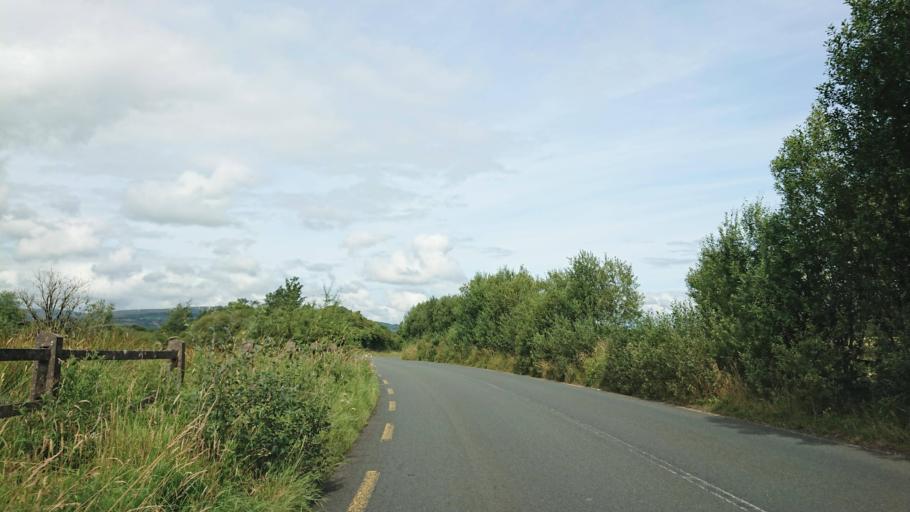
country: IE
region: Connaught
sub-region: County Leitrim
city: Carrick-on-Shannon
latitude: 54.0706
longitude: -8.0343
